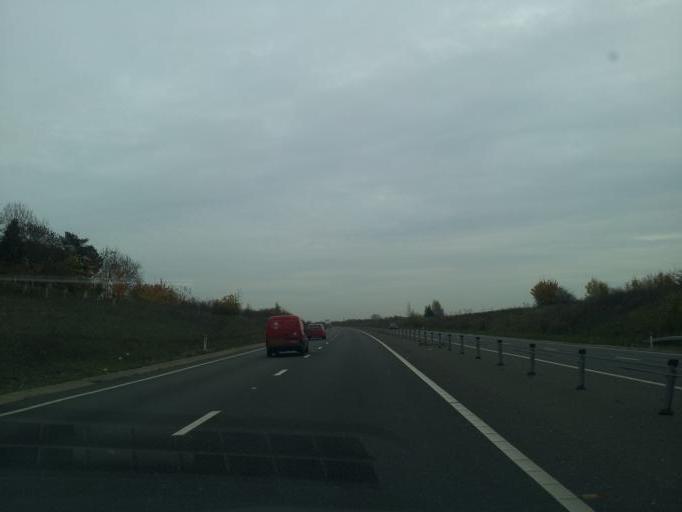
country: GB
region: England
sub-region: Cambridgeshire
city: Comberton
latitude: 52.2207
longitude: -0.0462
